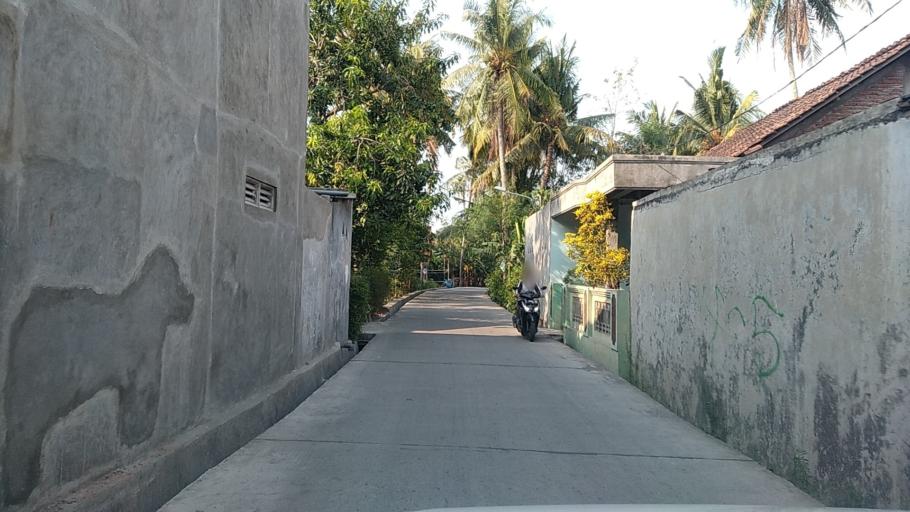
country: ID
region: Central Java
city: Mranggen
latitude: -6.9748
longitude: 110.4989
